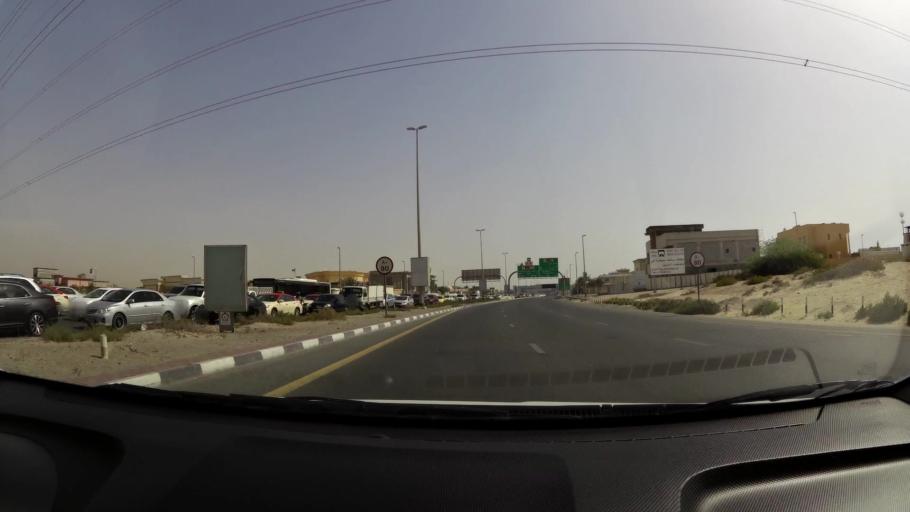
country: AE
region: Ash Shariqah
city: Sharjah
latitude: 25.2692
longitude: 55.3951
